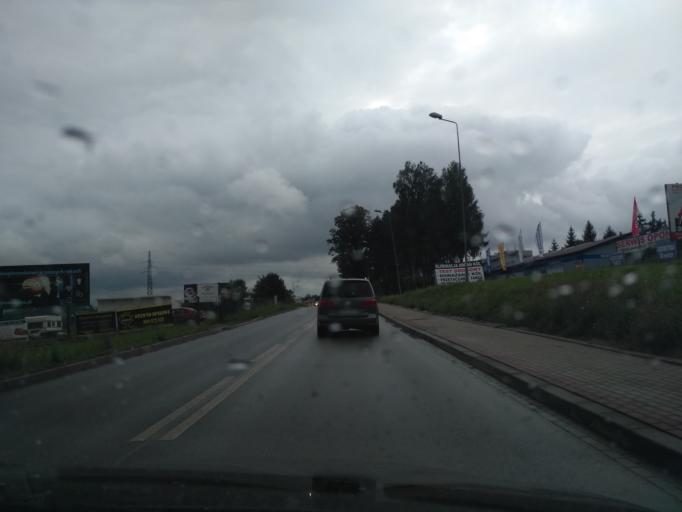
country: PL
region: Subcarpathian Voivodeship
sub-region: Powiat krosnienski
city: Korczyna
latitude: 49.7061
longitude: 21.7882
